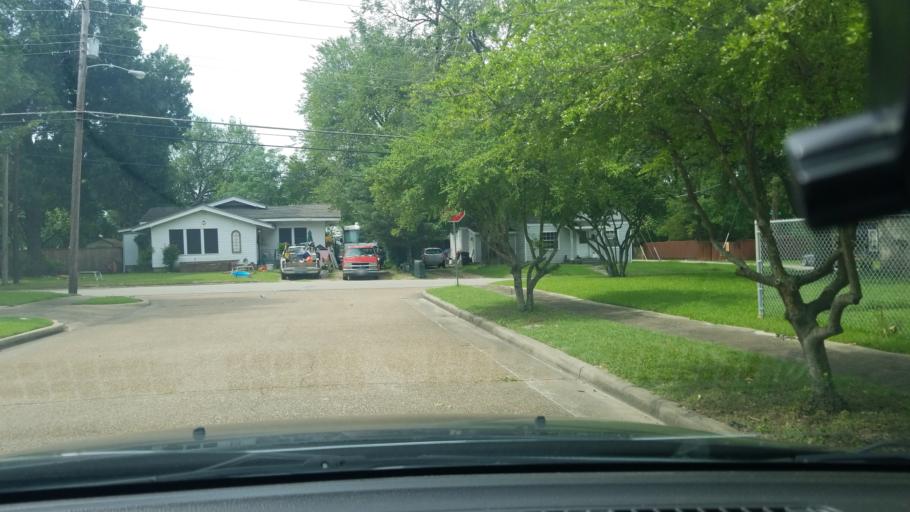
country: US
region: Texas
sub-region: Dallas County
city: Mesquite
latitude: 32.7689
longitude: -96.5951
